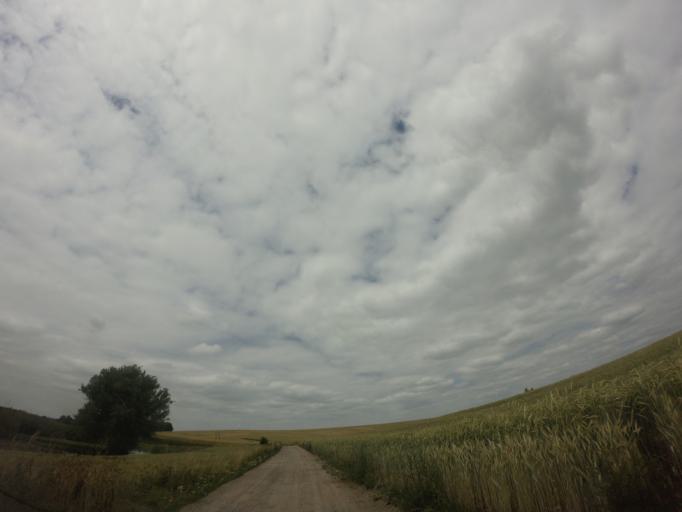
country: PL
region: West Pomeranian Voivodeship
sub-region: Powiat choszczenski
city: Krzecin
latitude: 53.0780
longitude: 15.5217
